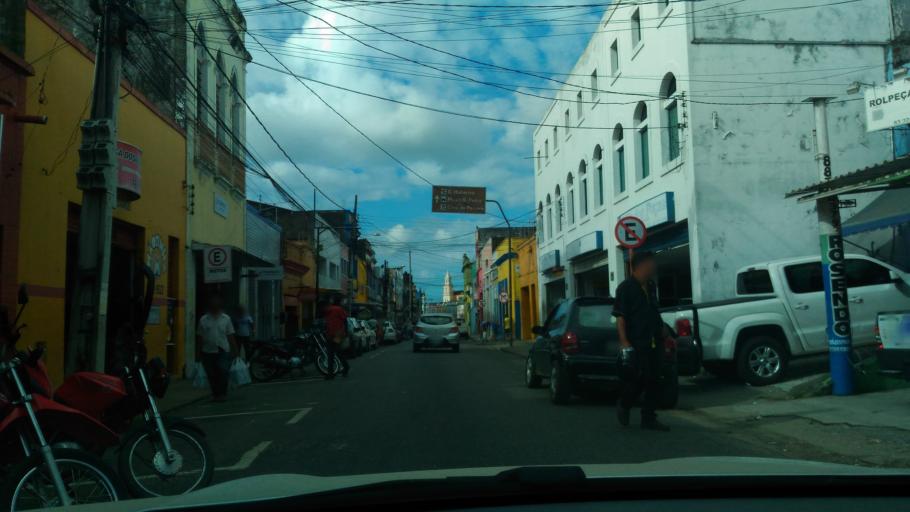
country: BR
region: Paraiba
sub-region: Joao Pessoa
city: Joao Pessoa
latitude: -7.1173
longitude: -34.8890
